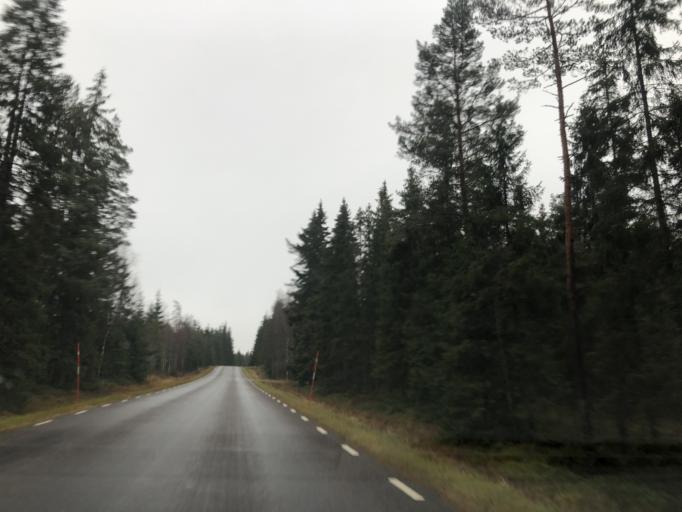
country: SE
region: Vaestra Goetaland
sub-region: Ulricehamns Kommun
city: Ulricehamn
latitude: 57.7408
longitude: 13.5381
